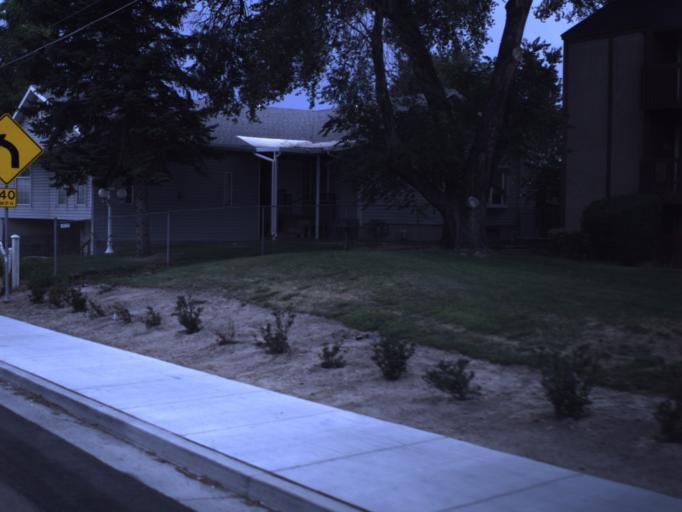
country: US
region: Utah
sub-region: Salt Lake County
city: Millcreek
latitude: 40.6710
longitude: -111.8717
